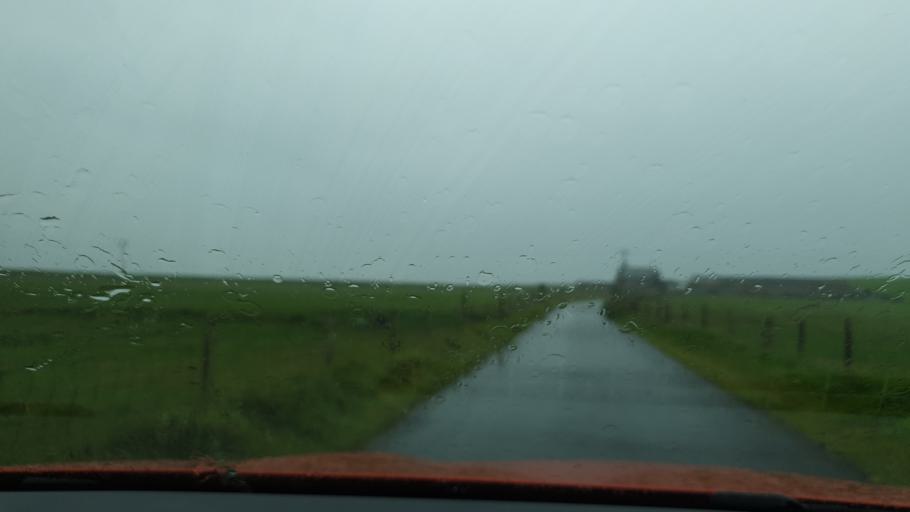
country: GB
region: England
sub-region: Cumbria
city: Barrow in Furness
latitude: 54.0574
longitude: -3.2132
